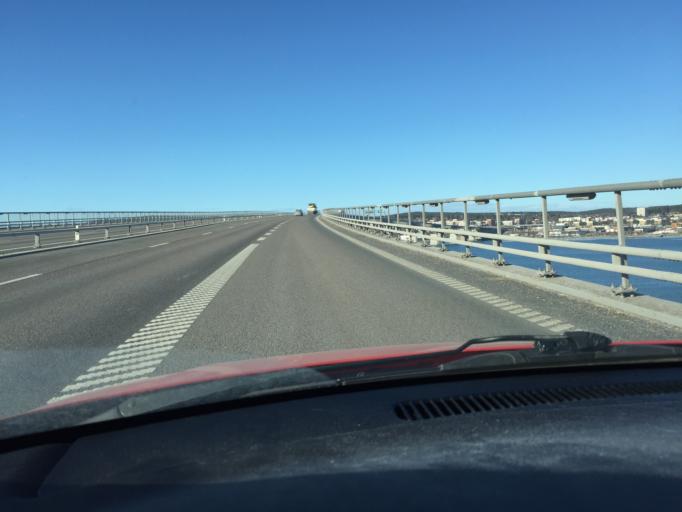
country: SE
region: Vaesternorrland
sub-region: Sundsvalls Kommun
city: Sundsvall
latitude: 62.3838
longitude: 17.3482
